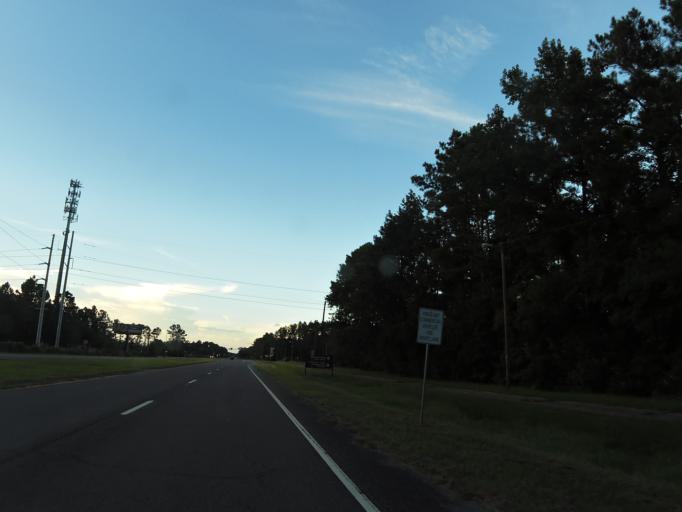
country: US
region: Georgia
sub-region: Camden County
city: Kings Bay Base
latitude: 30.7801
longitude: -81.5764
